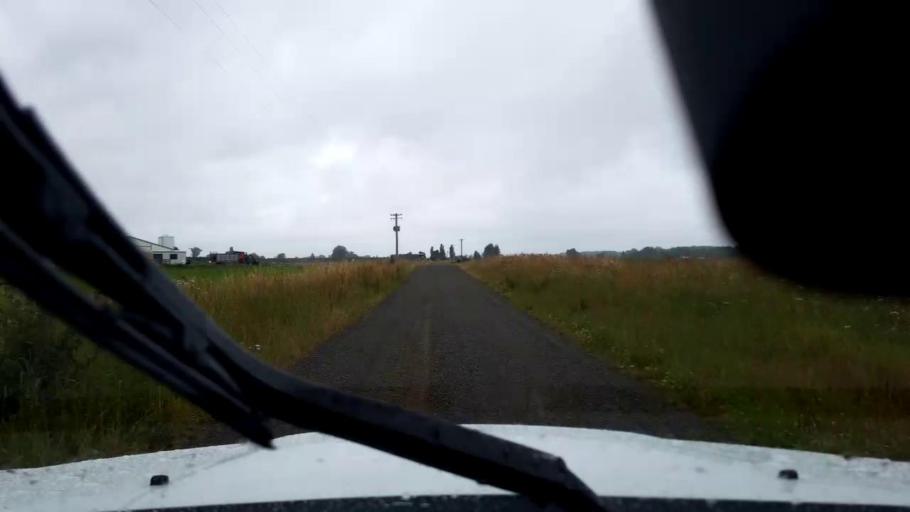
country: NZ
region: Canterbury
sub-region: Timaru District
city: Pleasant Point
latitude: -44.2534
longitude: 171.2064
